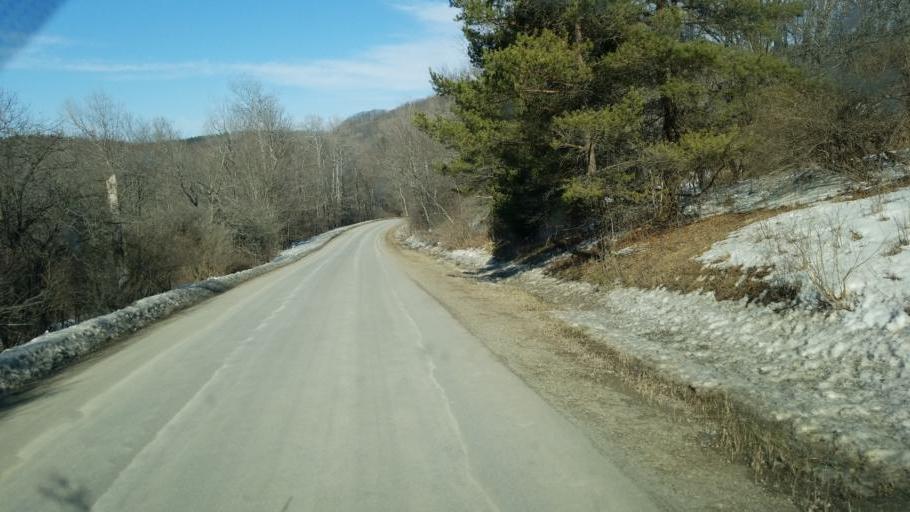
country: US
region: New York
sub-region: Allegany County
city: Andover
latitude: 42.1487
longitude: -77.7706
